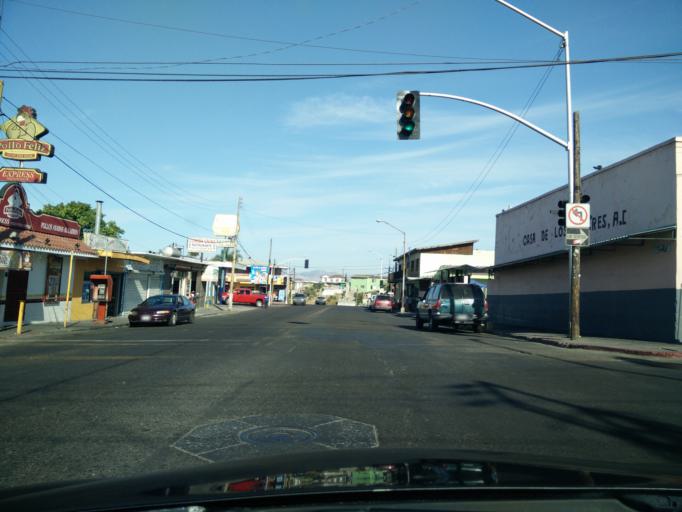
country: MX
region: Baja California
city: Tijuana
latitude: 32.5262
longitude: -117.0549
